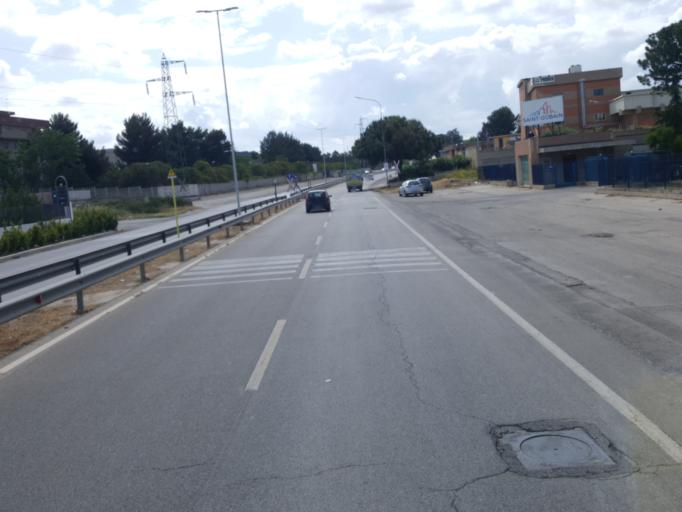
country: IT
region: Apulia
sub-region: Provincia di Bari
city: San Paolo
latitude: 41.1160
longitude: 16.8116
